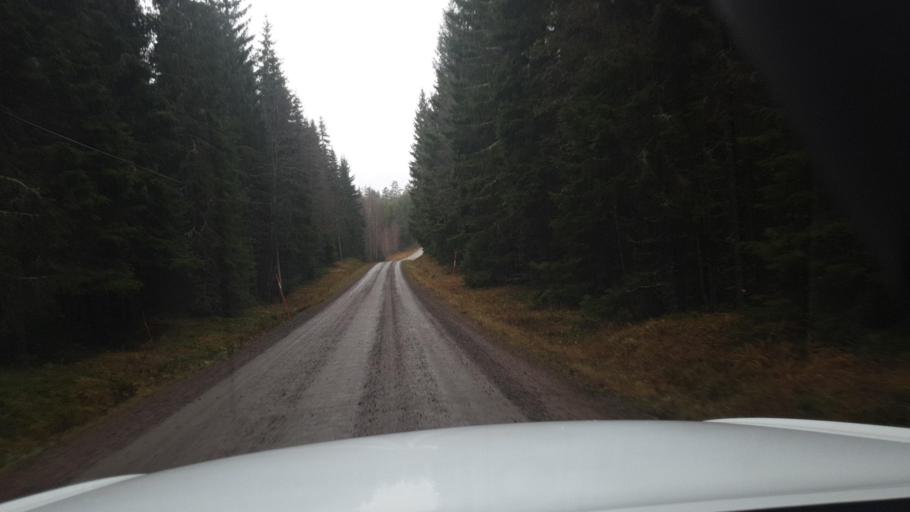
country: SE
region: Vaermland
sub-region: Eda Kommun
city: Charlottenberg
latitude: 59.8949
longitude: 12.3762
